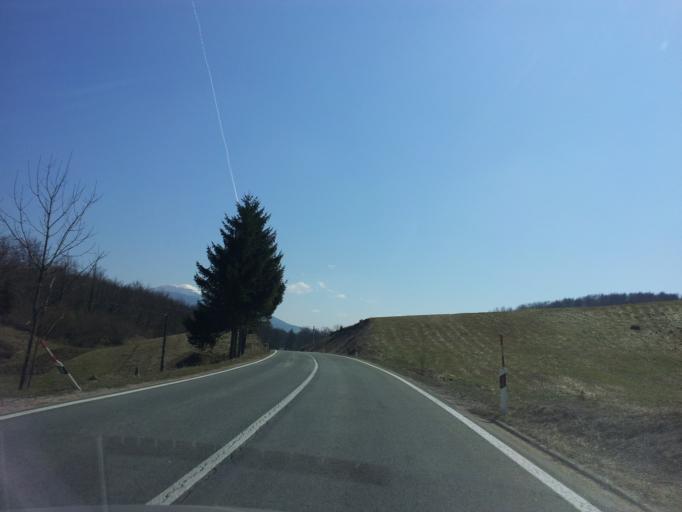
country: HR
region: Licko-Senjska
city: Jezerce
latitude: 44.8497
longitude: 15.6529
